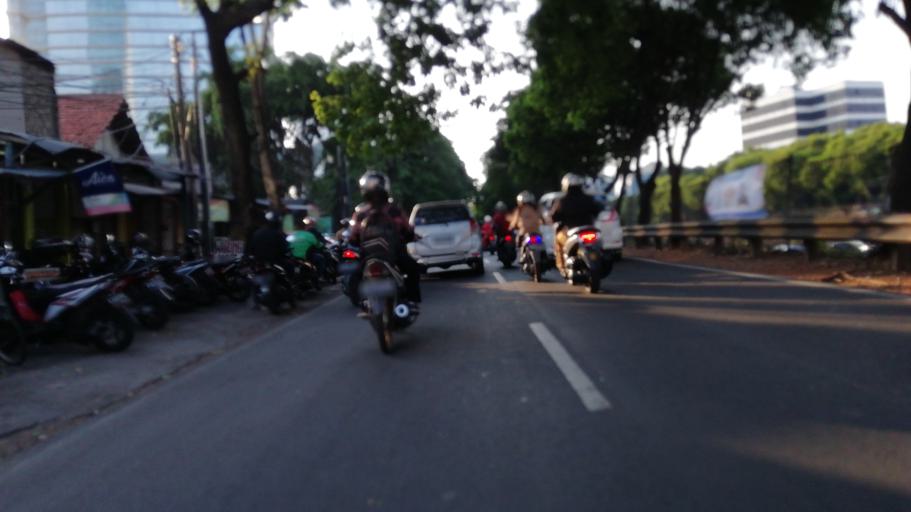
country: ID
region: Jakarta Raya
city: Jakarta
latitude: -6.2994
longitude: 106.8326
